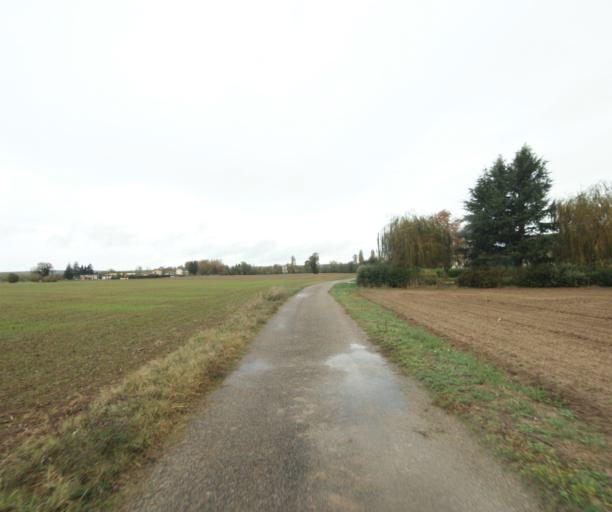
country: FR
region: Rhone-Alpes
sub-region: Departement de l'Ain
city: Pont-de-Vaux
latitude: 46.4657
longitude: 4.8990
